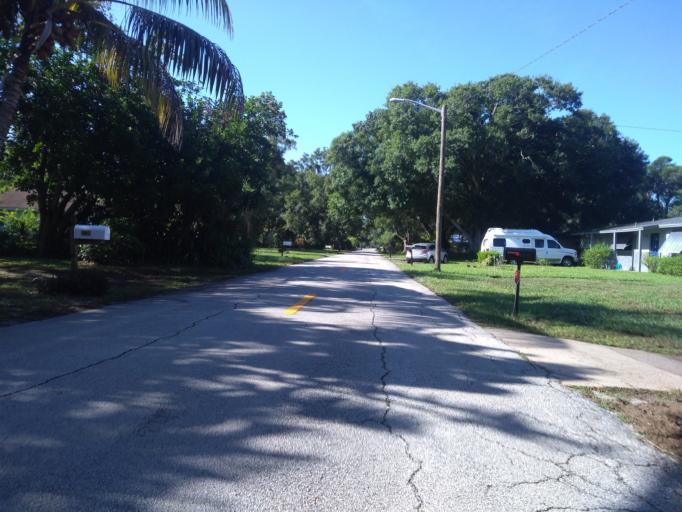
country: US
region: Florida
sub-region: Indian River County
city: Vero Beach
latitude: 27.6337
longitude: -80.4122
